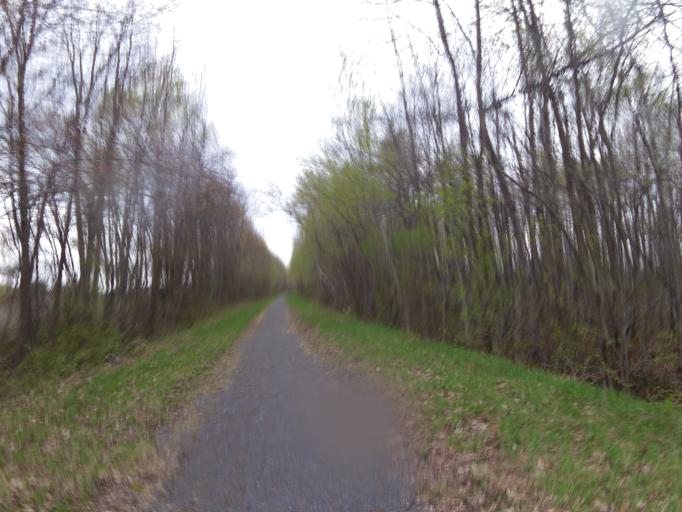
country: CA
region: Ontario
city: Bourget
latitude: 45.4415
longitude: -75.1492
